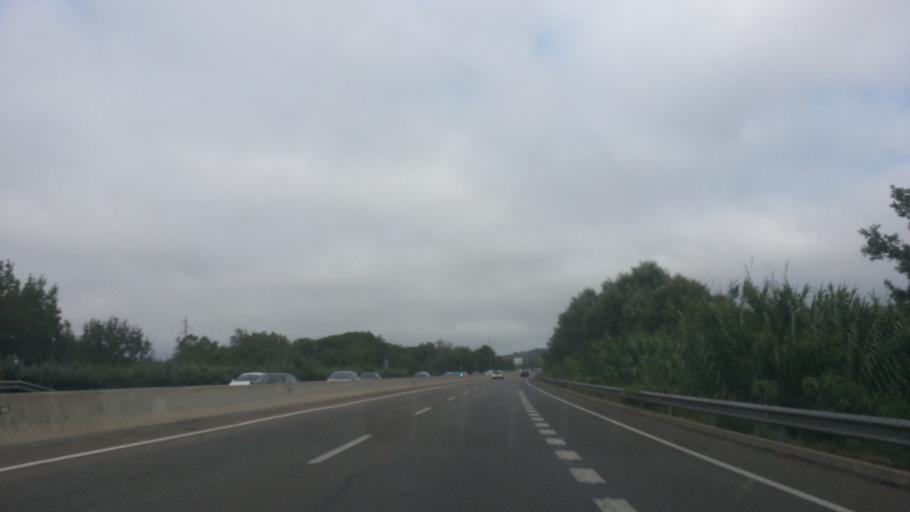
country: ES
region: Catalonia
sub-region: Provincia de Girona
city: Santa Cristina d'Aro
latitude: 41.8083
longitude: 3.0080
